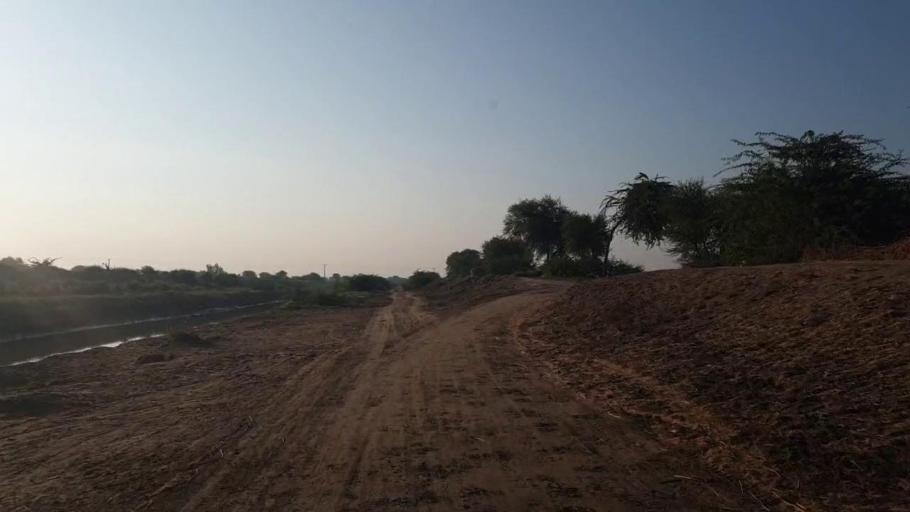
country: PK
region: Sindh
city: Badin
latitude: 24.6340
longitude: 68.7946
